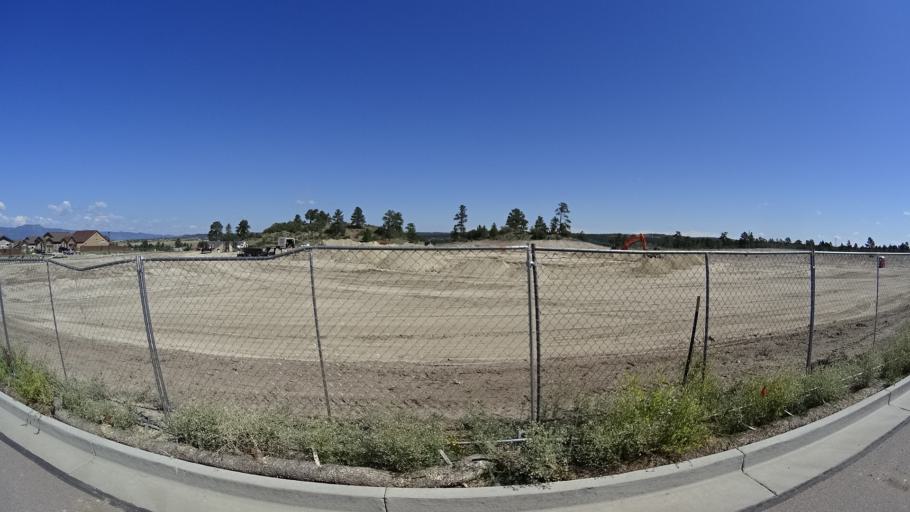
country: US
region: Colorado
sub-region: El Paso County
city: Black Forest
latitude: 38.9922
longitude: -104.7593
